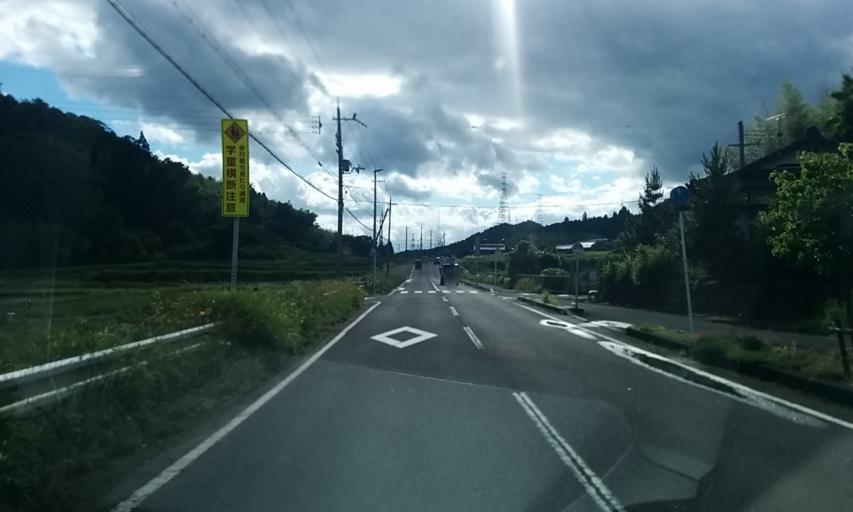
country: JP
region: Kyoto
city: Ayabe
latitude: 35.3542
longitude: 135.2854
